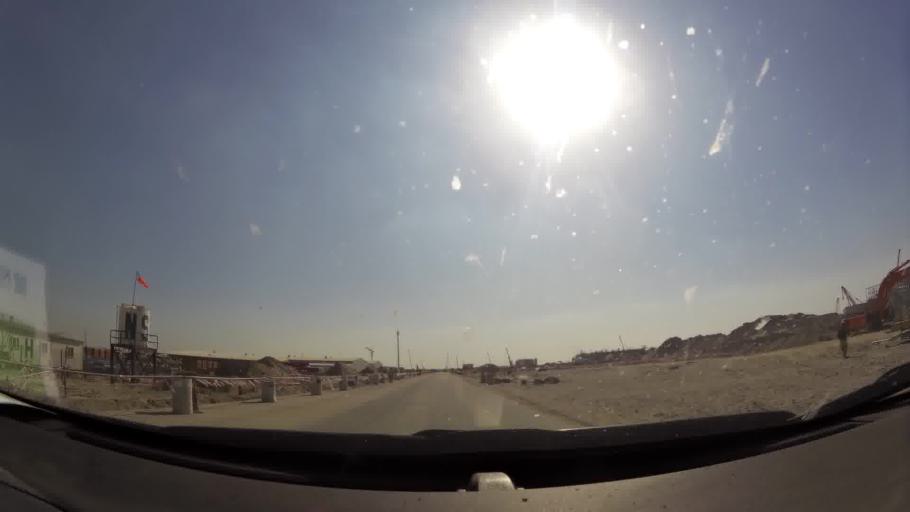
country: SA
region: Eastern Province
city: Al Khafji
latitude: 28.7083
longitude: 48.3404
